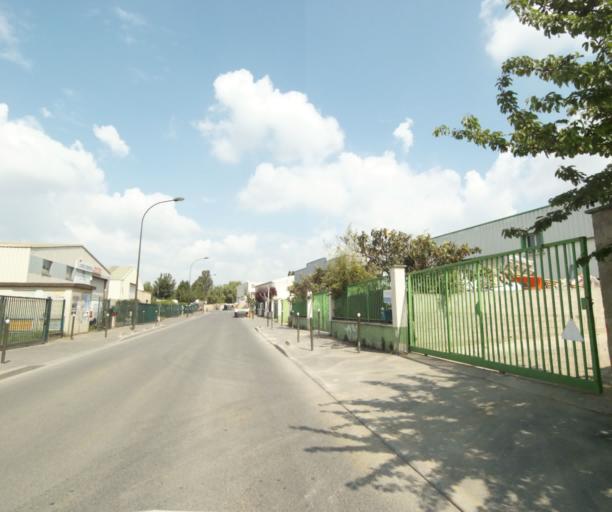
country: FR
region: Ile-de-France
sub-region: Departement du Val-d'Oise
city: Cormeilles-en-Parisis
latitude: 48.9592
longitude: 2.2078
